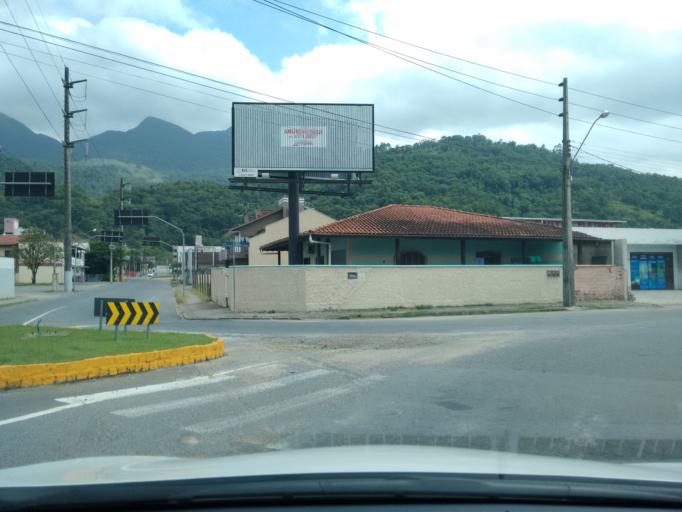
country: BR
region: Santa Catarina
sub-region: Jaragua Do Sul
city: Jaragua do Sul
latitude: -26.4884
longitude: -49.0565
